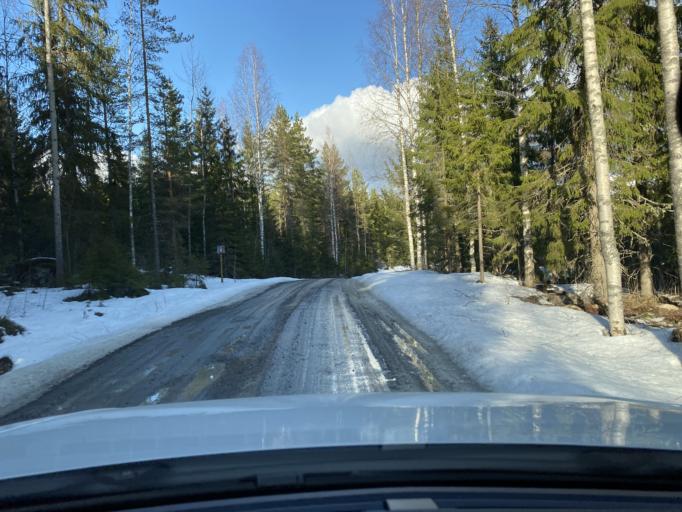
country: FI
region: Pirkanmaa
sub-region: Lounais-Pirkanmaa
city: Mouhijaervi
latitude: 61.4604
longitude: 22.9523
